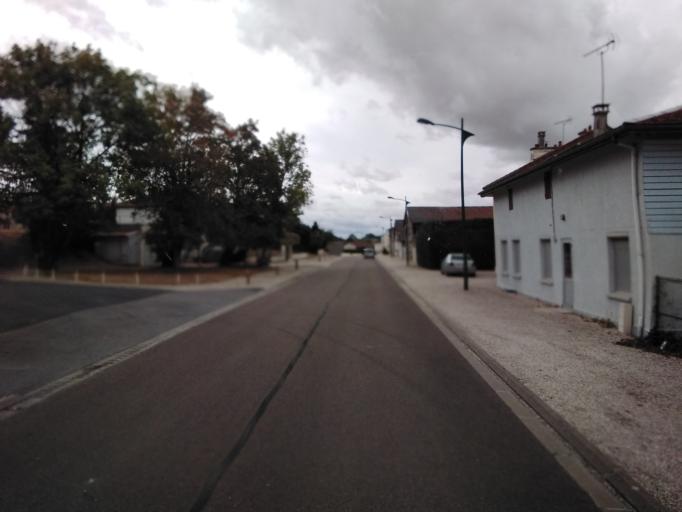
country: FR
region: Champagne-Ardenne
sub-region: Departement de la Marne
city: Frignicourt
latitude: 48.5581
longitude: 4.5244
